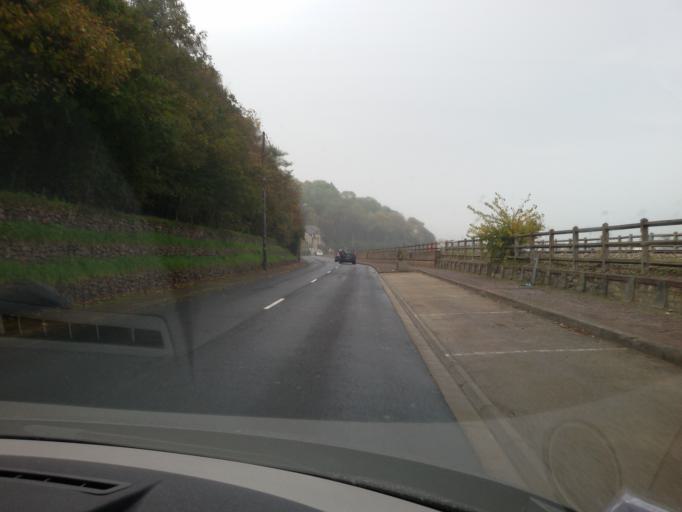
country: FR
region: Lower Normandy
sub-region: Departement du Calvados
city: Houlgate
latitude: 49.2976
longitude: -0.0862
